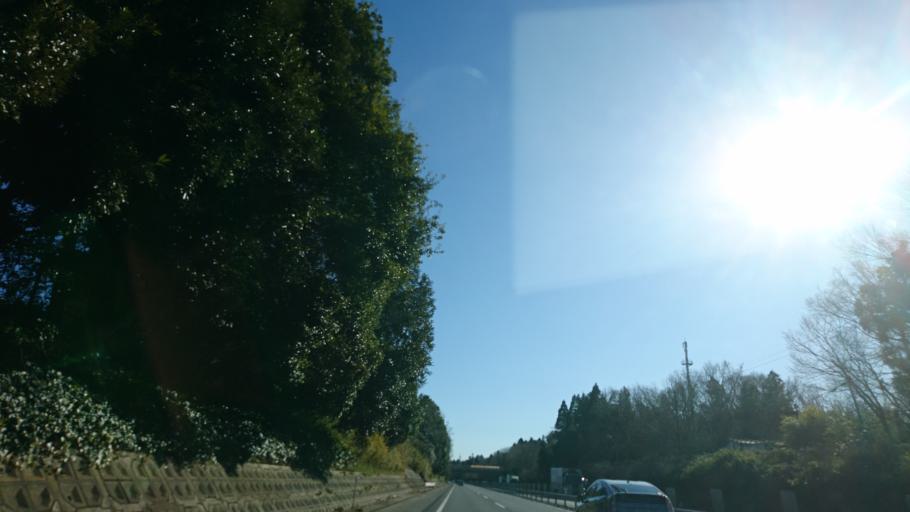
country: JP
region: Chiba
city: Chiba
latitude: 35.5778
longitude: 140.1933
